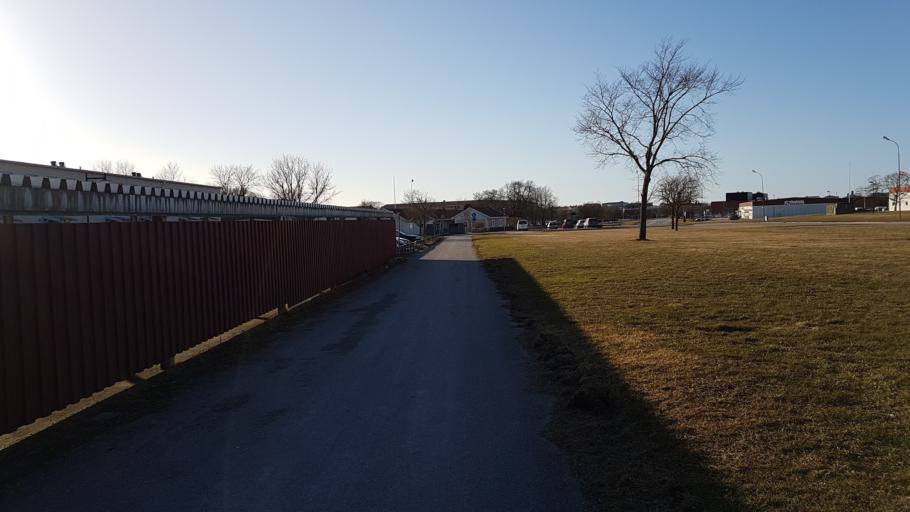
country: SE
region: Gotland
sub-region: Gotland
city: Visby
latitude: 57.6411
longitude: 18.3212
